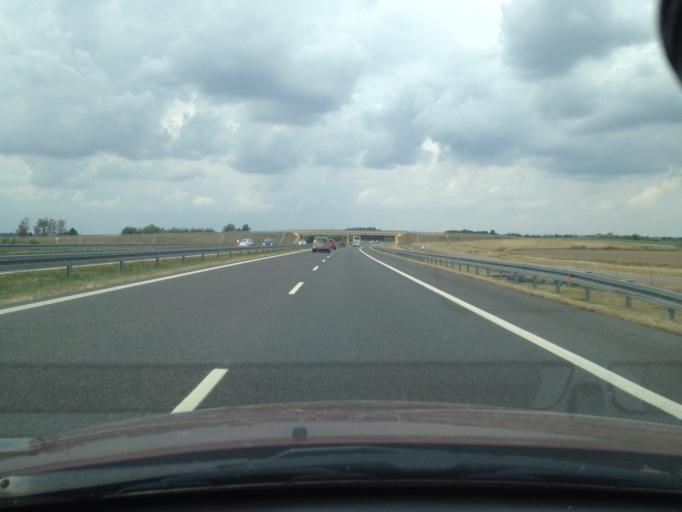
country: PL
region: West Pomeranian Voivodeship
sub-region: Powiat pyrzycki
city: Lipiany
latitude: 52.9569
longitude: 14.9350
